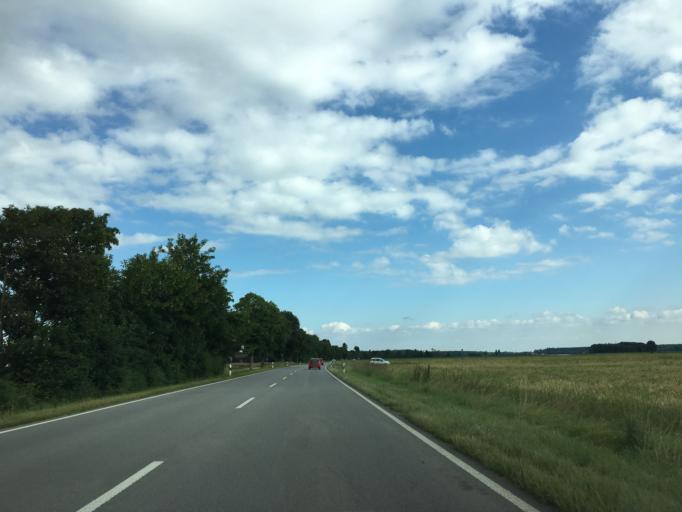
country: DE
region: Bavaria
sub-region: Upper Bavaria
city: Otterfing
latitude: 47.9329
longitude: 11.6542
